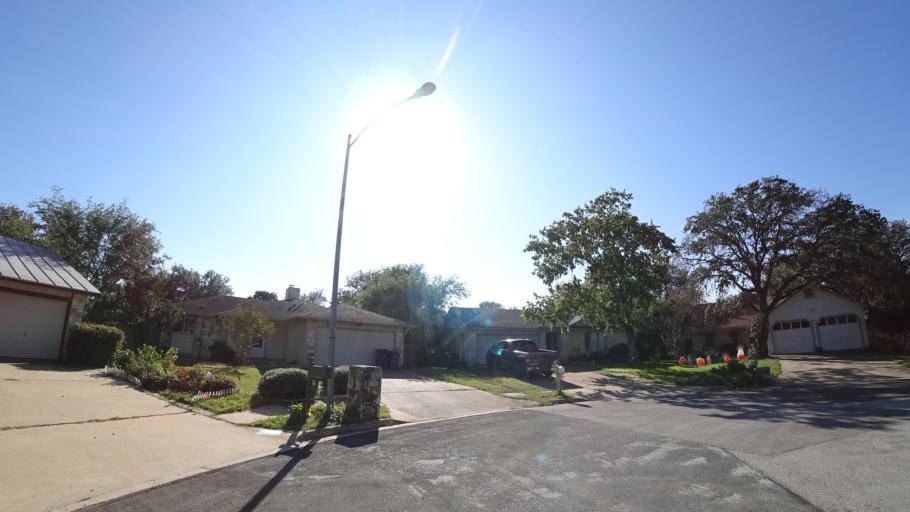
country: US
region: Texas
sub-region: Travis County
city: Shady Hollow
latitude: 30.2120
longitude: -97.8507
